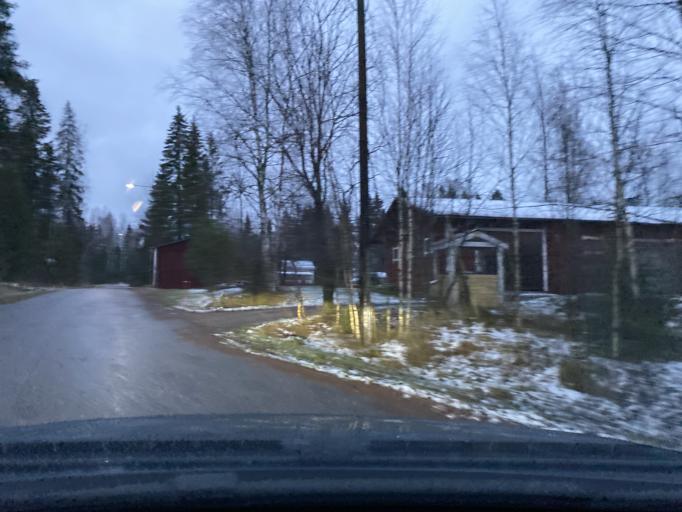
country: FI
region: Pirkanmaa
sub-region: Lounais-Pirkanmaa
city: Punkalaidun
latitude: 61.1424
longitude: 22.9507
